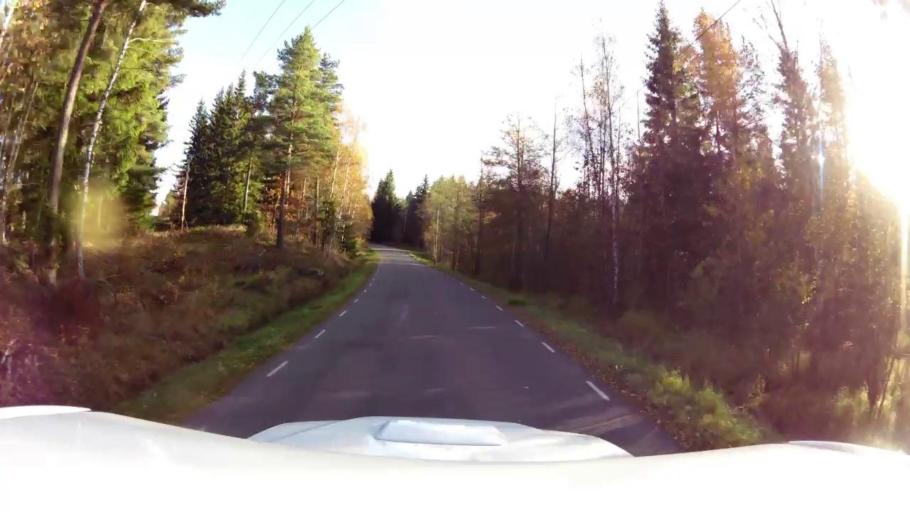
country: SE
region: OEstergoetland
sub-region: Linkopings Kommun
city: Vikingstad
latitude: 58.2619
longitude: 15.4544
